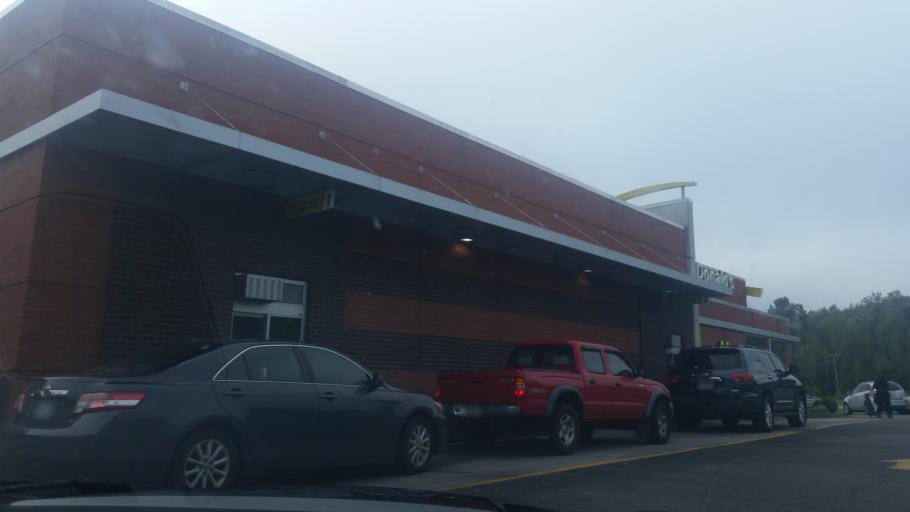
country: US
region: Virginia
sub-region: Henrico County
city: Sandston
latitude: 37.5118
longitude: -77.1928
